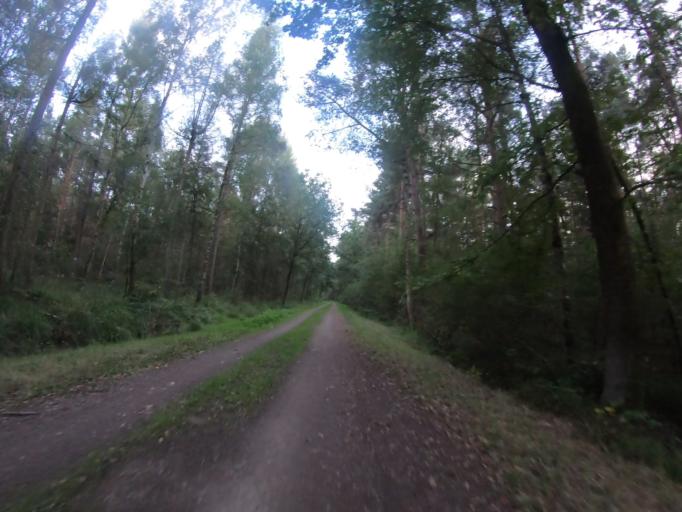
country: DE
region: Lower Saxony
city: Gifhorn
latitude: 52.5132
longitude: 10.5607
